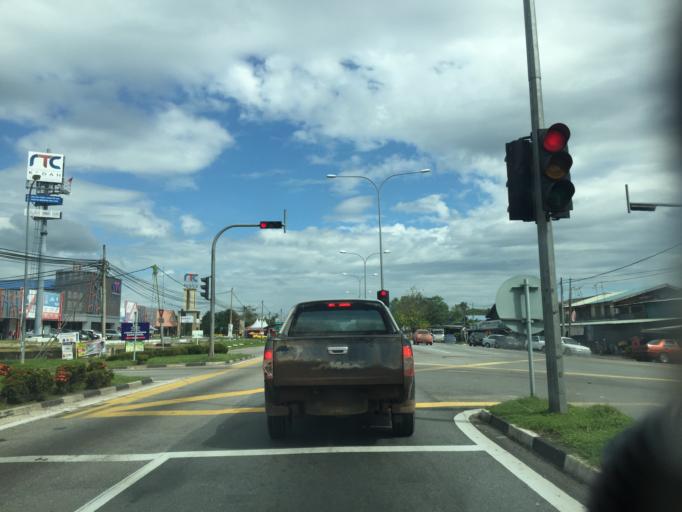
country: MY
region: Kedah
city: Jitra
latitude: 6.3611
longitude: 100.4225
